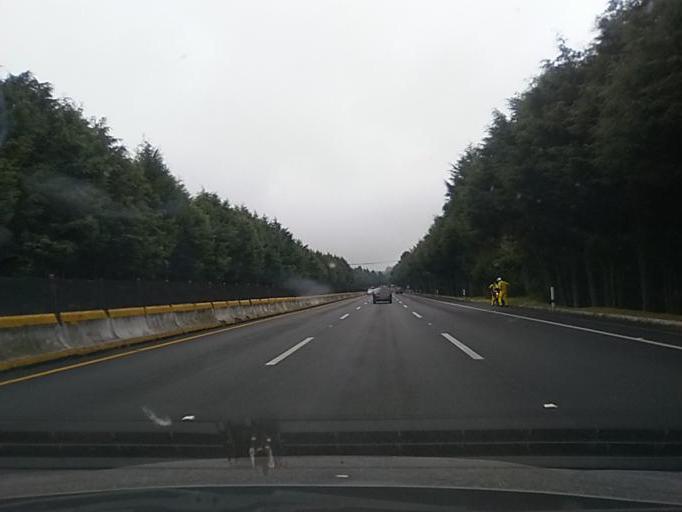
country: MX
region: Morelos
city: Tres Marias
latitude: 19.1414
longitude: -99.1639
